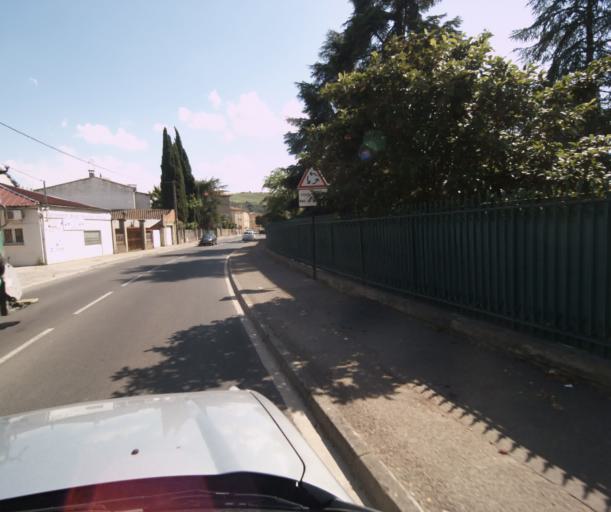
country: FR
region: Languedoc-Roussillon
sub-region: Departement de l'Aude
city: Limoux
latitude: 43.0579
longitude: 2.2214
